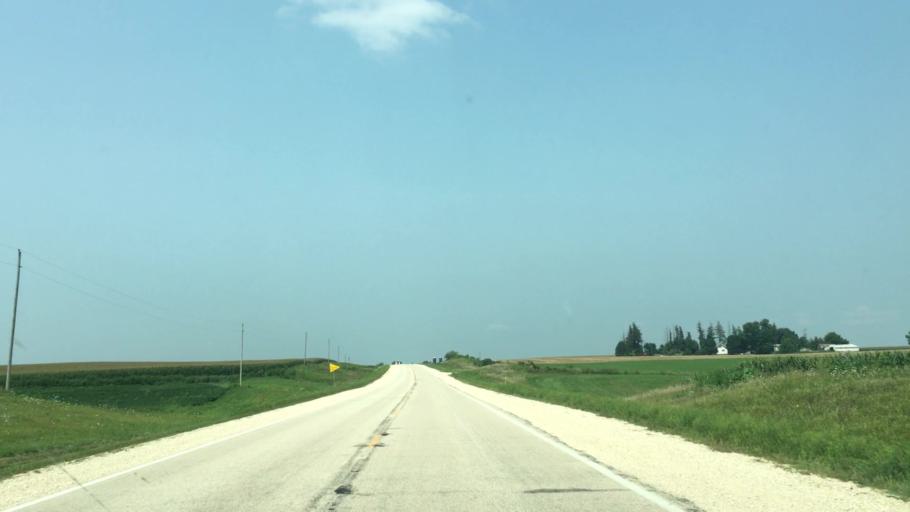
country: US
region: Iowa
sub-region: Fayette County
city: West Union
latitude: 42.9923
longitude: -91.8239
